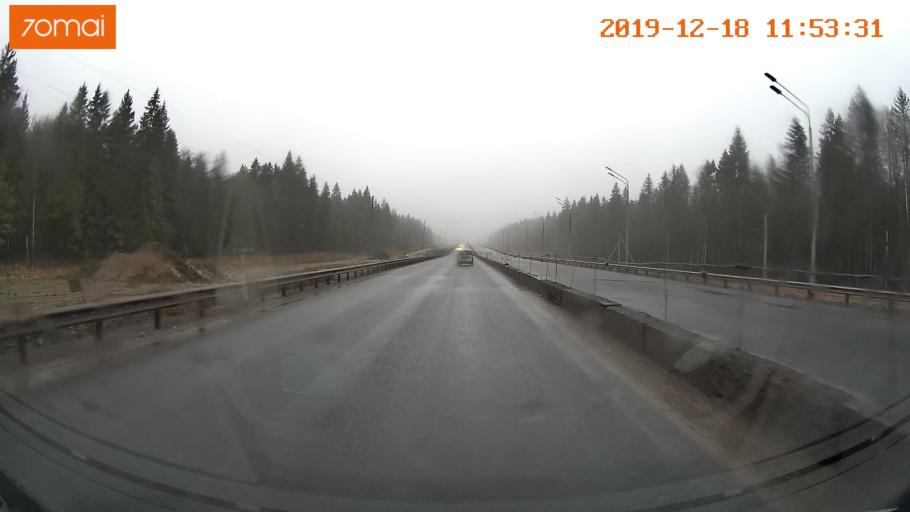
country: RU
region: Moskovskaya
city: Yershovo
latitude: 55.8053
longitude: 36.9198
